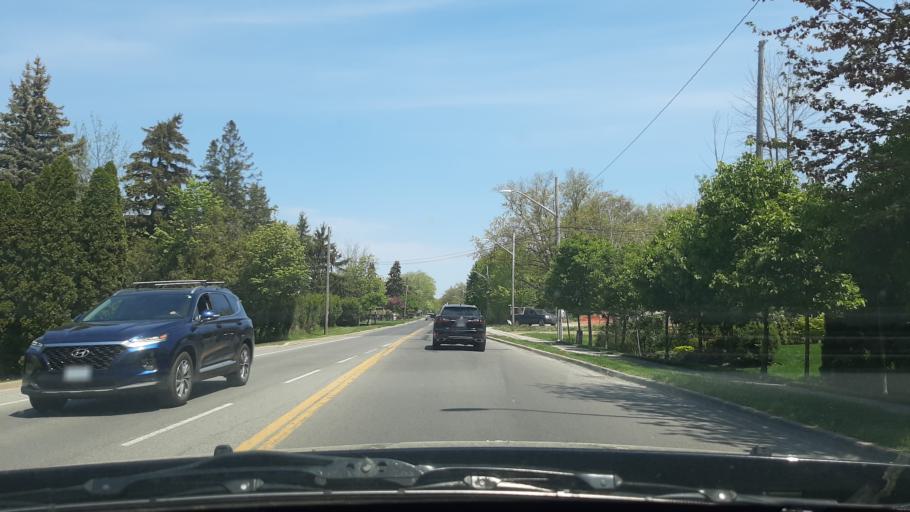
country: US
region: New York
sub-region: Niagara County
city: Youngstown
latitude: 43.2500
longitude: -79.0866
